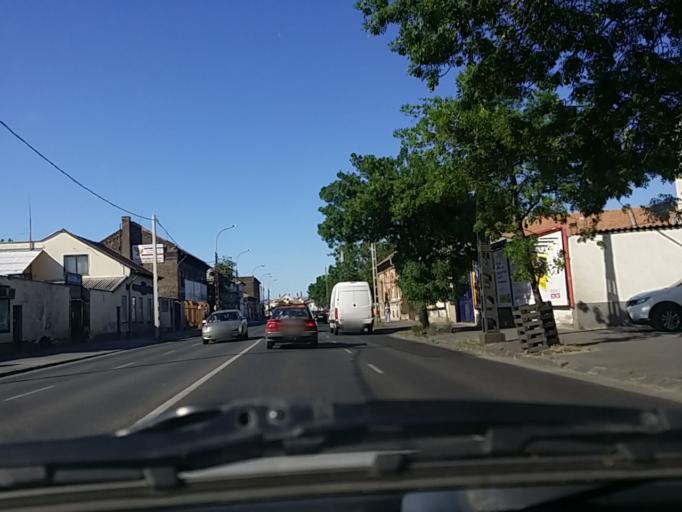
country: HU
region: Budapest
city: Budapest IV. keruelet
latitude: 47.5665
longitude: 19.0797
